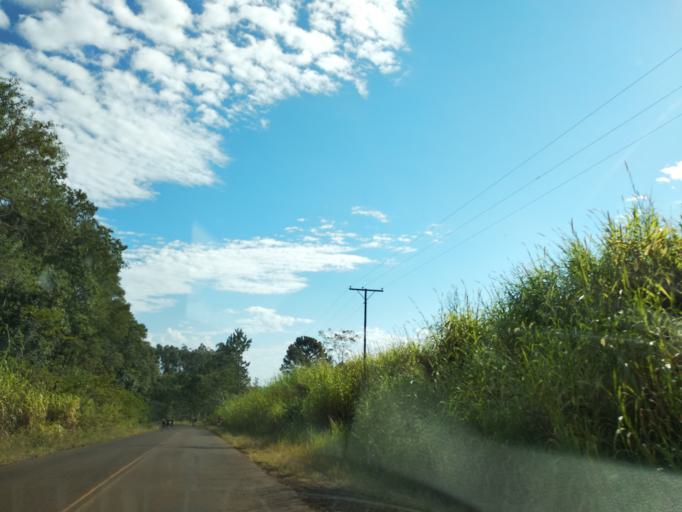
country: AR
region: Misiones
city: Aristobulo del Valle
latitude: -27.0702
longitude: -54.8269
